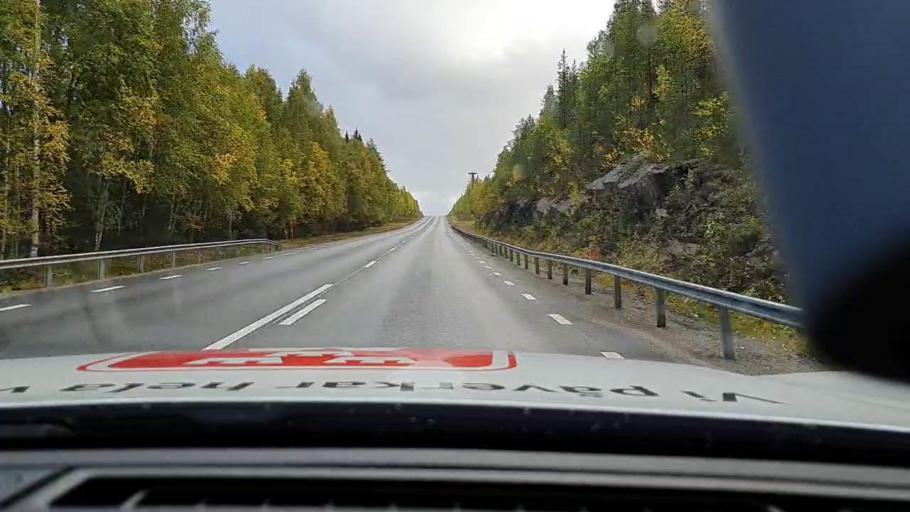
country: SE
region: Vaesterbotten
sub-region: Norsjo Kommun
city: Norsjoe
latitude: 64.9727
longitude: 19.7437
